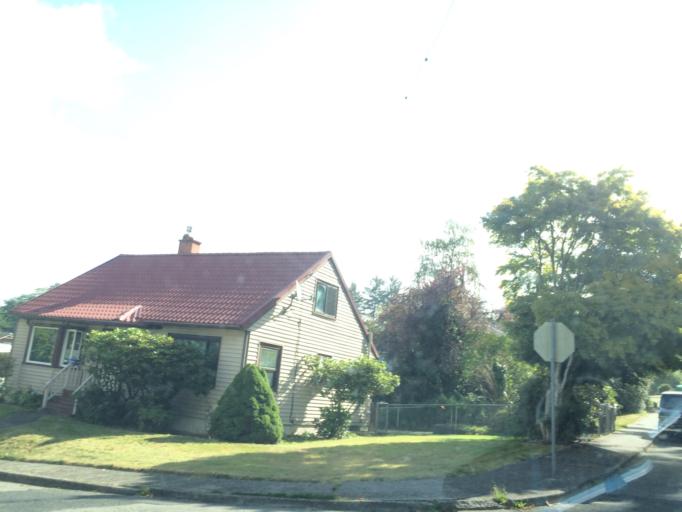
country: US
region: Oregon
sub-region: Clatsop County
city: Astoria
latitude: 46.1883
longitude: -123.8046
